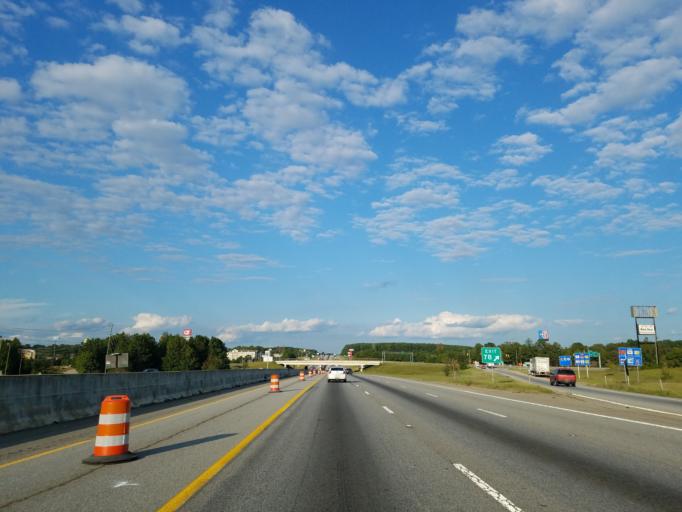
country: US
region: South Carolina
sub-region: Spartanburg County
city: Spartanburg
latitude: 35.0158
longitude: -81.9006
